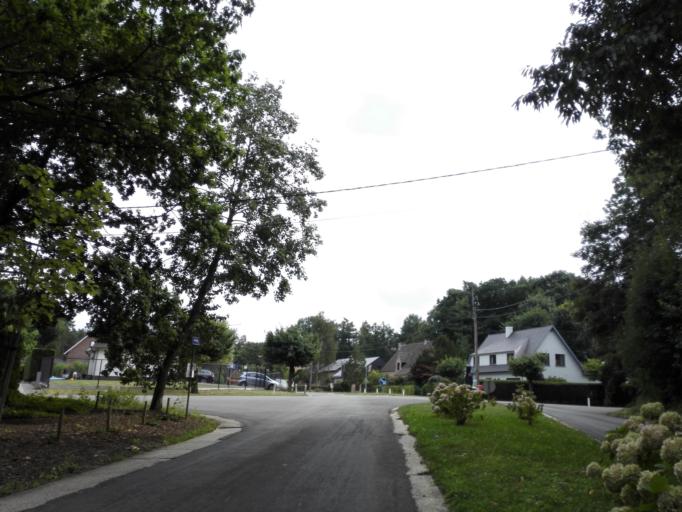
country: BE
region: Flanders
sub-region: Provincie Vlaams-Brabant
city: Holsbeek
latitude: 50.9016
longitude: 4.7807
